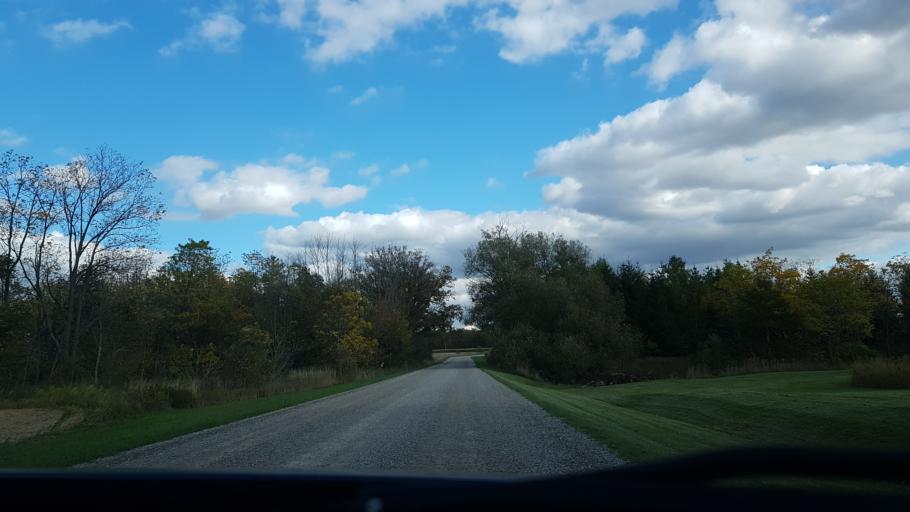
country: CA
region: Ontario
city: South Huron
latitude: 43.1067
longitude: -81.6116
